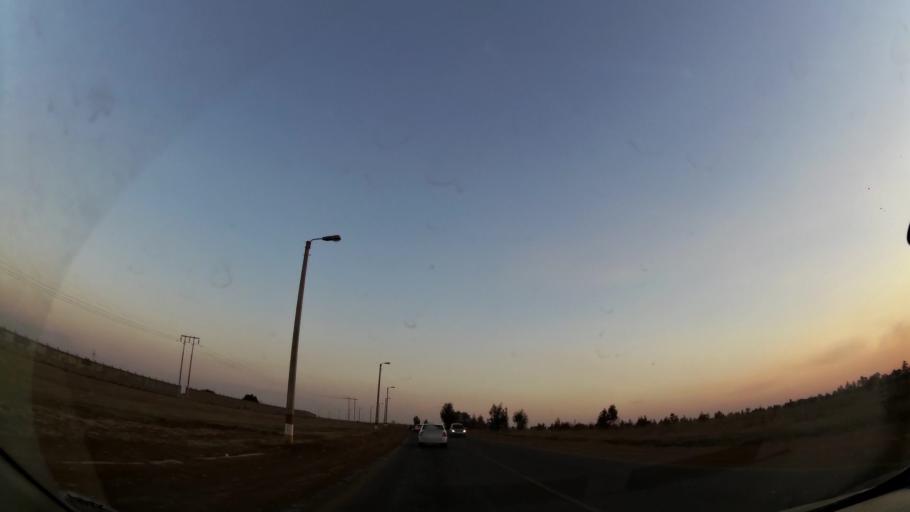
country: ZA
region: Gauteng
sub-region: Ekurhuleni Metropolitan Municipality
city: Springs
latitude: -26.3494
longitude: 28.4140
